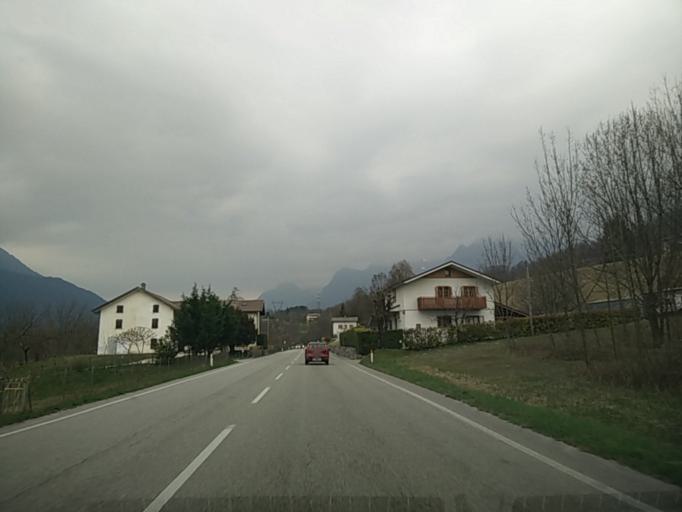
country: IT
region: Veneto
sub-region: Provincia di Belluno
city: Ponte nell'Alpi
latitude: 46.1598
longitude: 12.2676
